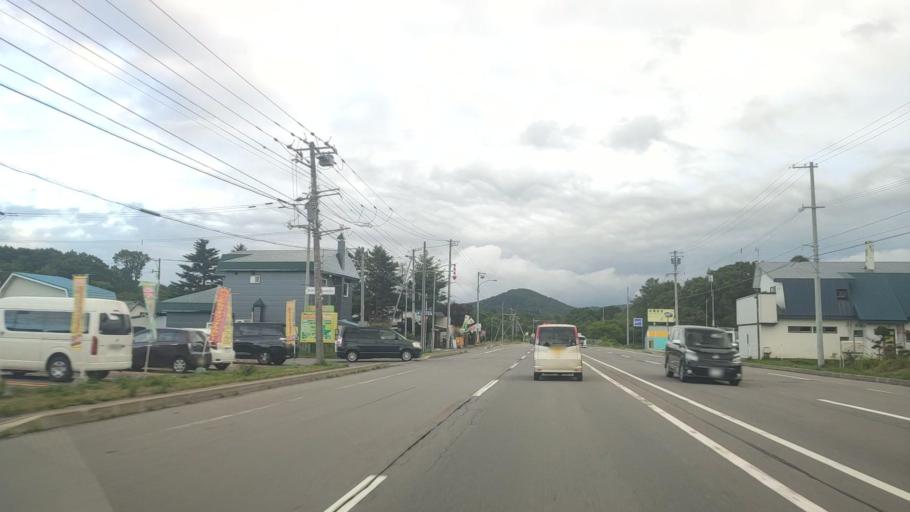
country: JP
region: Hokkaido
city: Nanae
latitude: 42.0029
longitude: 140.6336
